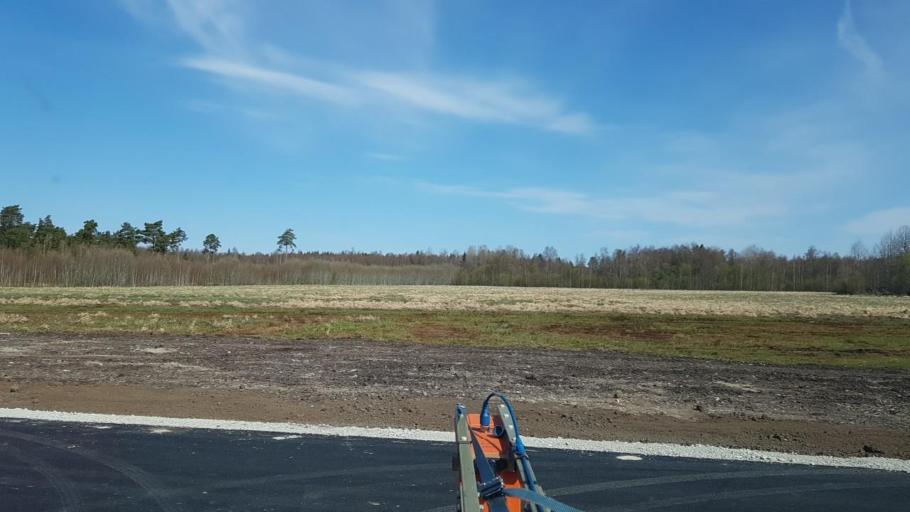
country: EE
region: Harju
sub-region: Kiili vald
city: Kiili
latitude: 59.3361
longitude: 24.7963
